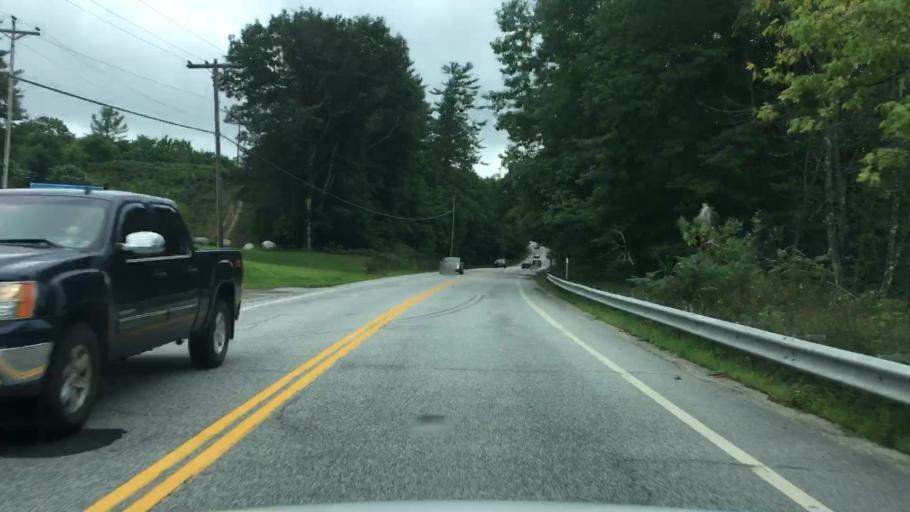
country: US
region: Maine
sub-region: Oxford County
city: Hiram
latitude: 43.8584
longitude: -70.7899
